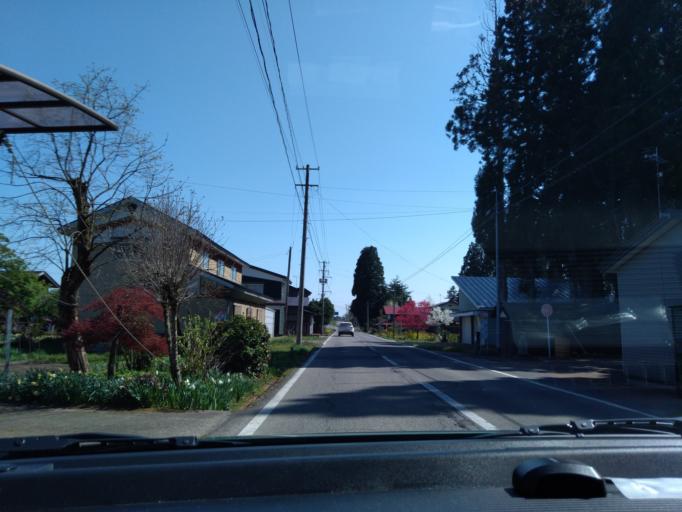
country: JP
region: Akita
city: Kakunodatemachi
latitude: 39.5475
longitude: 140.5858
